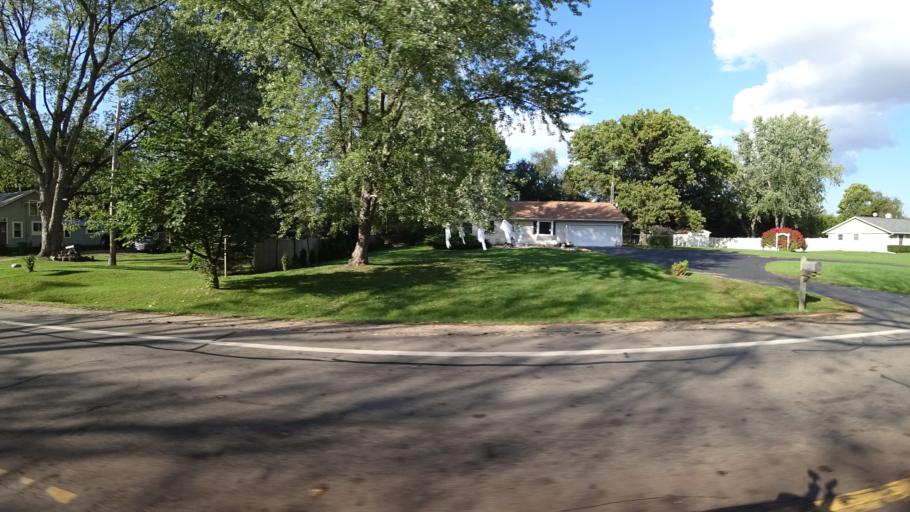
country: US
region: Michigan
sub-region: Saint Joseph County
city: Three Rivers
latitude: 41.9257
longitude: -85.5896
